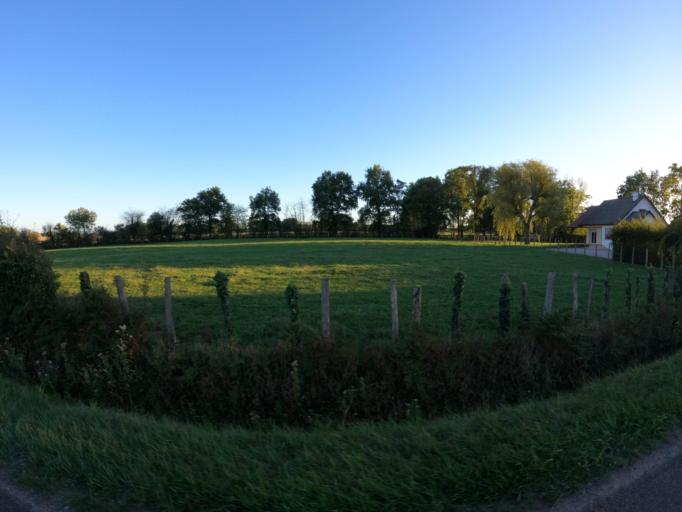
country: FR
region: Bourgogne
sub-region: Departement de Saone-et-Loire
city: Saint-Germain-du-Bois
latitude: 46.7514
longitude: 5.2668
